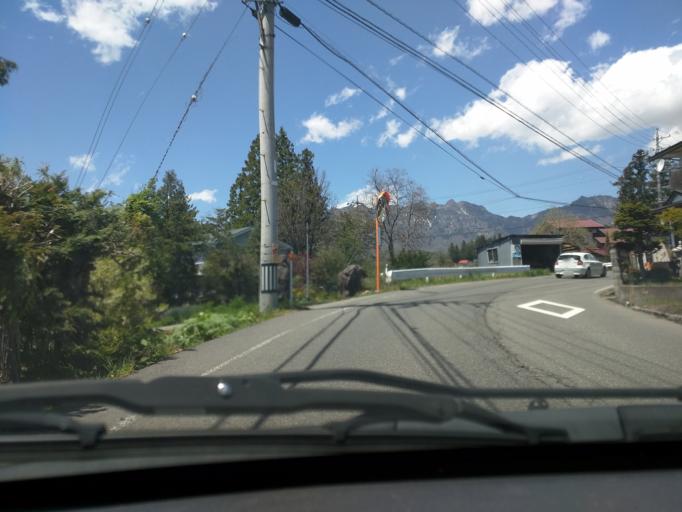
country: JP
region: Nagano
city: Nagano-shi
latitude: 36.7063
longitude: 138.0913
